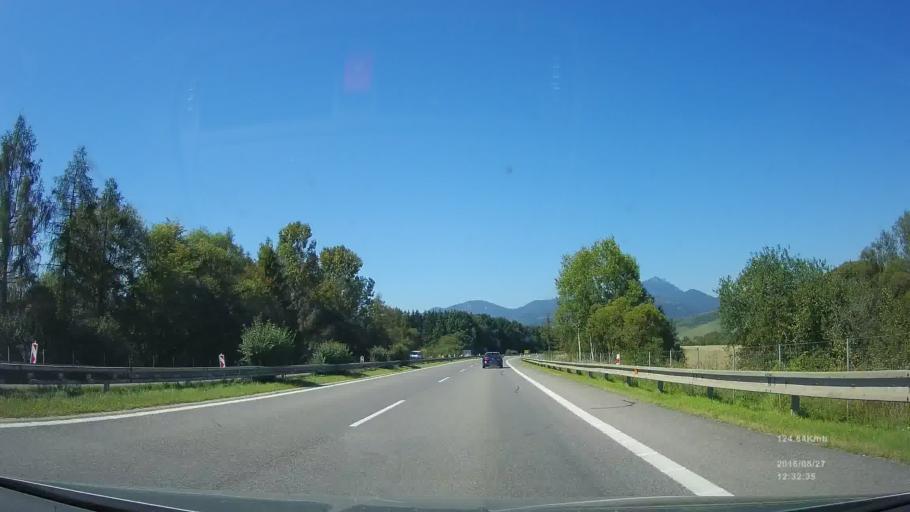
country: SK
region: Zilinsky
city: Ruzomberok
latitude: 49.0905
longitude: 19.4522
